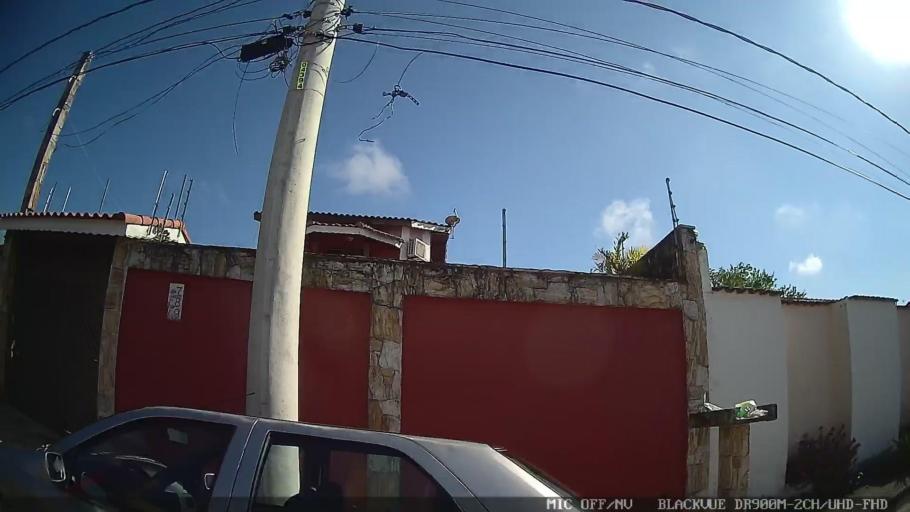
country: BR
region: Sao Paulo
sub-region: Peruibe
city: Peruibe
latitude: -24.2832
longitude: -46.9587
